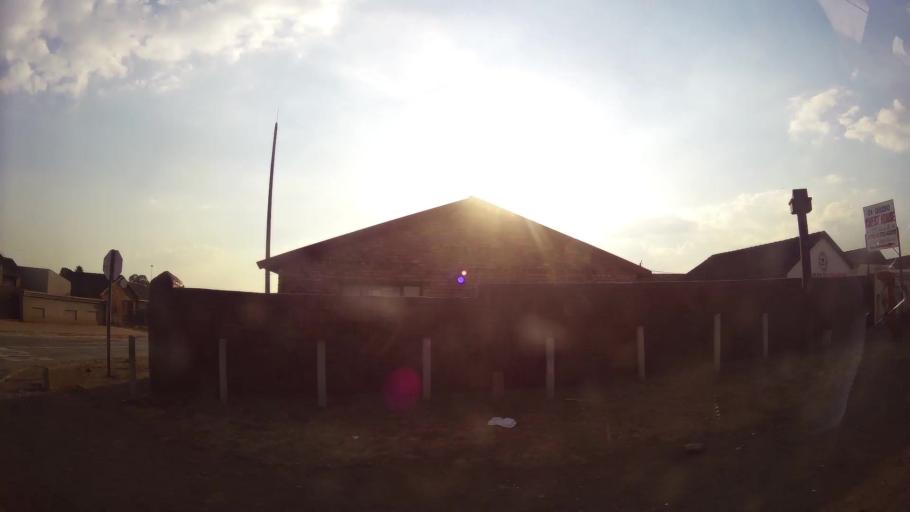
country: ZA
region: Gauteng
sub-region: Ekurhuleni Metropolitan Municipality
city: Germiston
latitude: -26.3484
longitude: 28.2136
